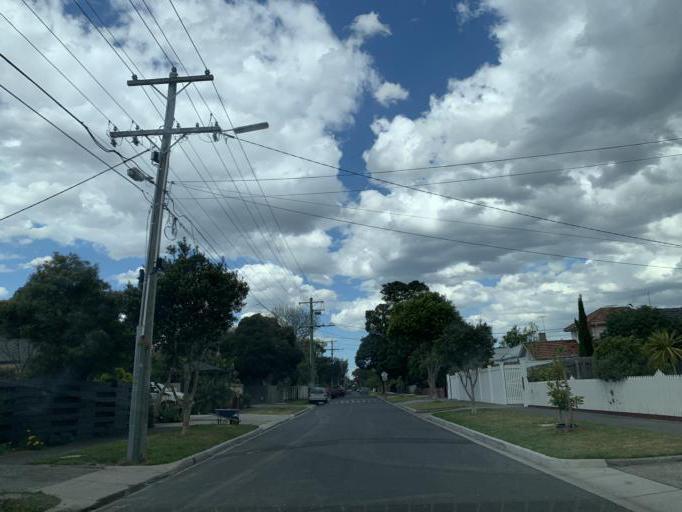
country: AU
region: Victoria
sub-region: Bayside
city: Hampton
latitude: -37.9426
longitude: 145.0141
